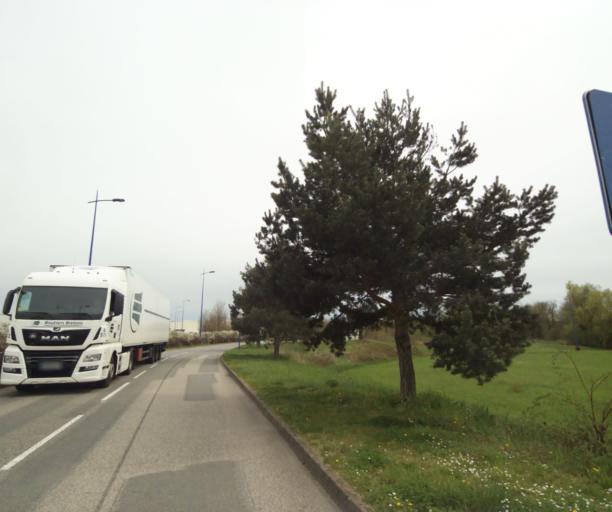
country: FR
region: Bourgogne
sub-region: Departement de Saone-et-Loire
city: Charnay-les-Macon
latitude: 46.2838
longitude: 4.7842
